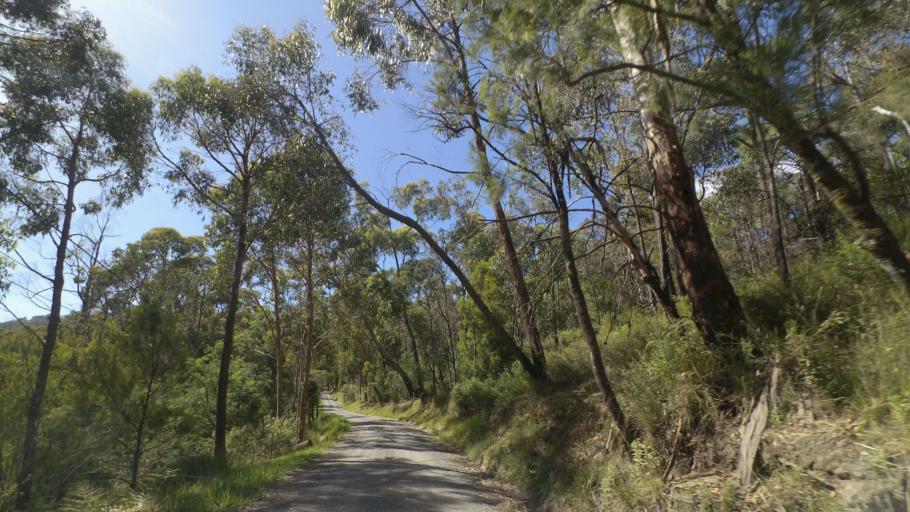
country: AU
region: Victoria
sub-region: Yarra Ranges
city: Kalorama
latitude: -37.8058
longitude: 145.3666
